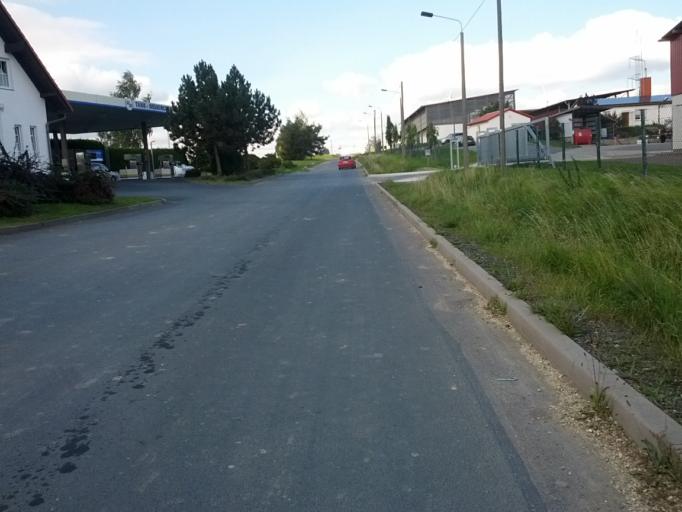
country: DE
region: Thuringia
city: Bischofroda
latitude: 51.0258
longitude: 10.3354
